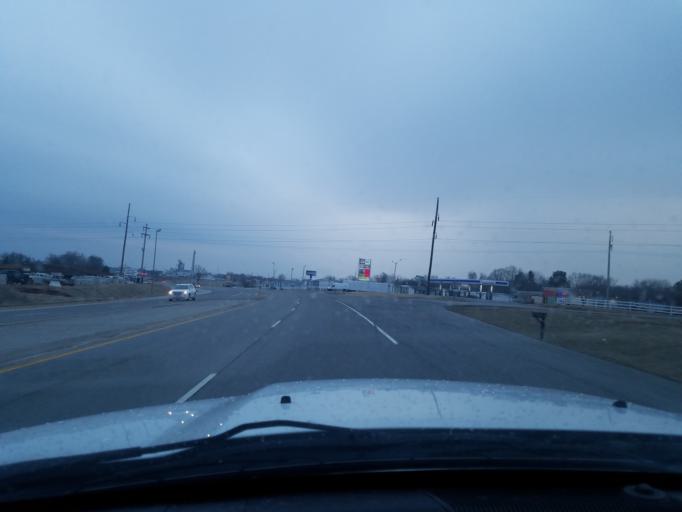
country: US
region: Kentucky
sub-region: Warren County
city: Bowling Green
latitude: 36.9540
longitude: -86.5039
